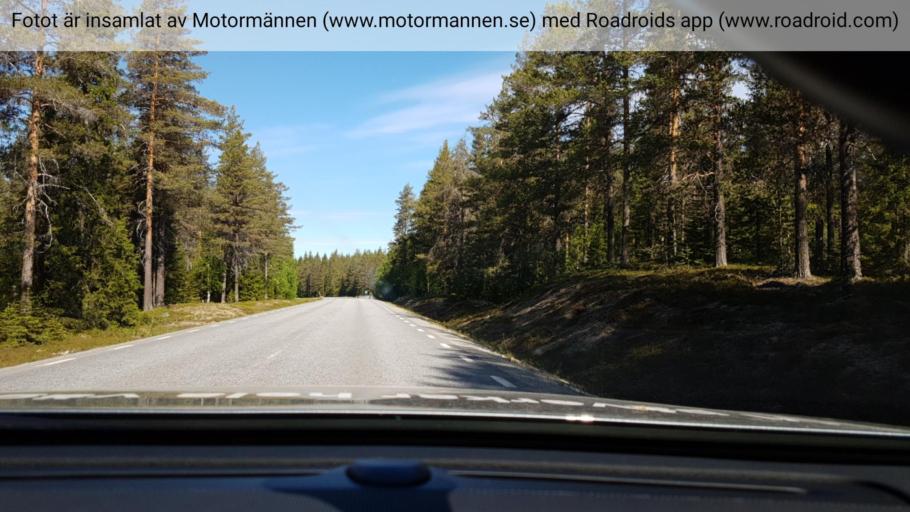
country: SE
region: Vaesterbotten
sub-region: Bjurholms Kommun
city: Bjurholm
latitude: 63.9689
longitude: 18.8373
